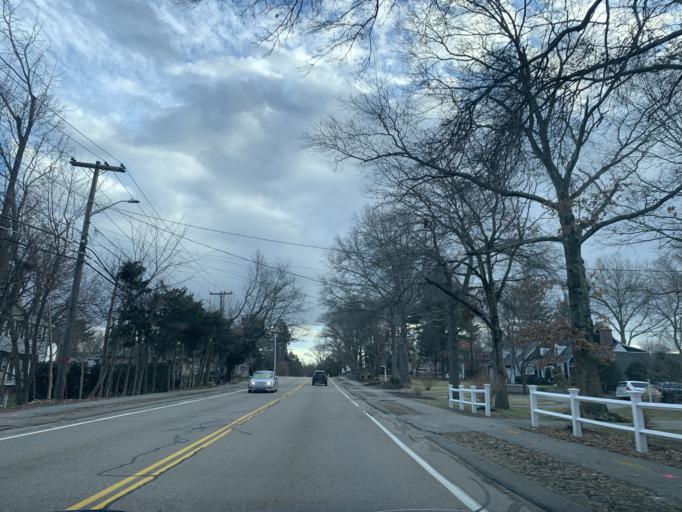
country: US
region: Massachusetts
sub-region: Norfolk County
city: Norwood
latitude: 42.1830
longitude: -71.1819
